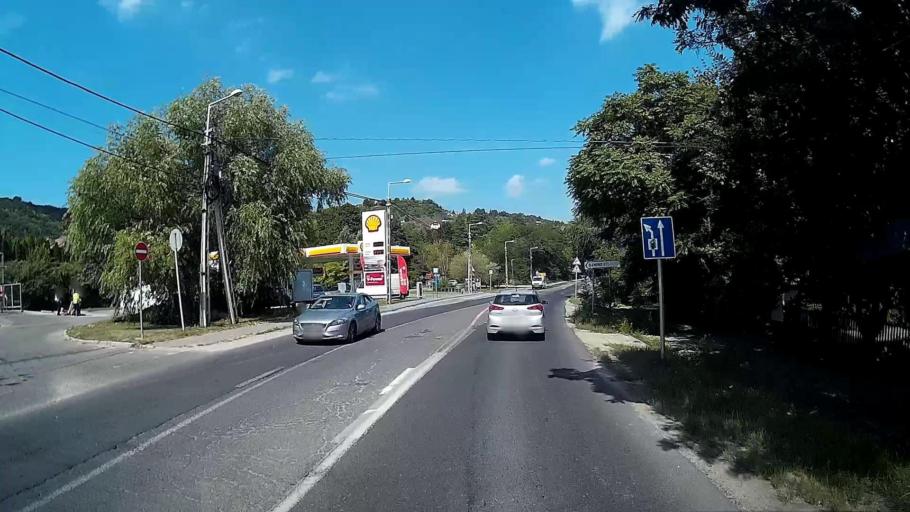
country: HU
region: Pest
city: Solymar
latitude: 47.5758
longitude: 18.9393
